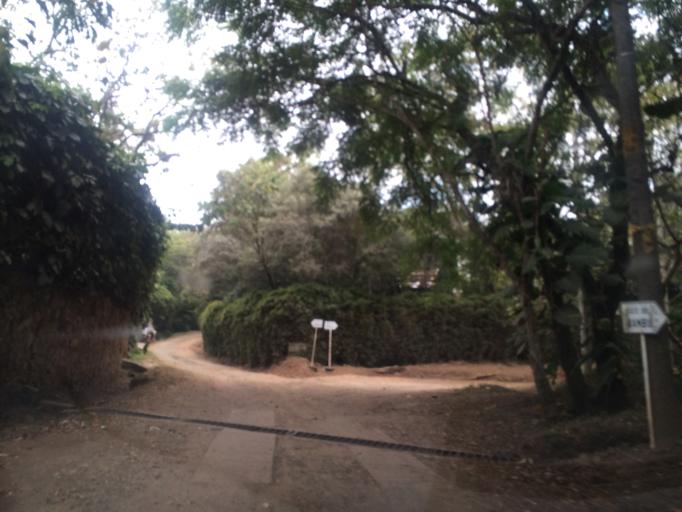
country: CO
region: Valle del Cauca
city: Cali
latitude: 3.4392
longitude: -76.5566
